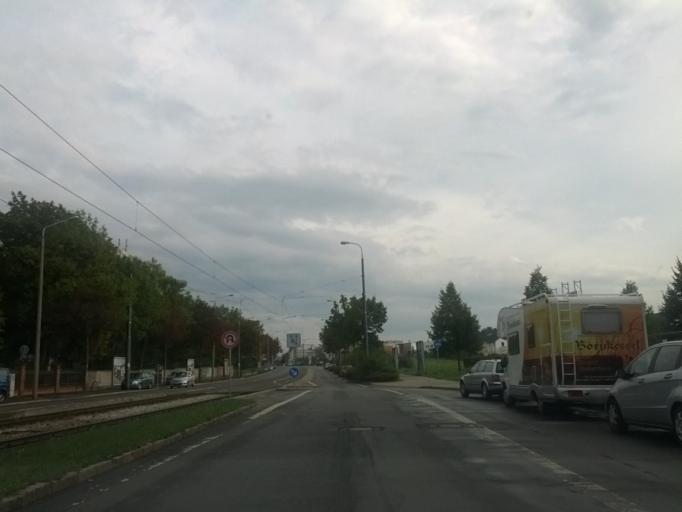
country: DE
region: Thuringia
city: Erfurt
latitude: 50.9904
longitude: 11.0124
